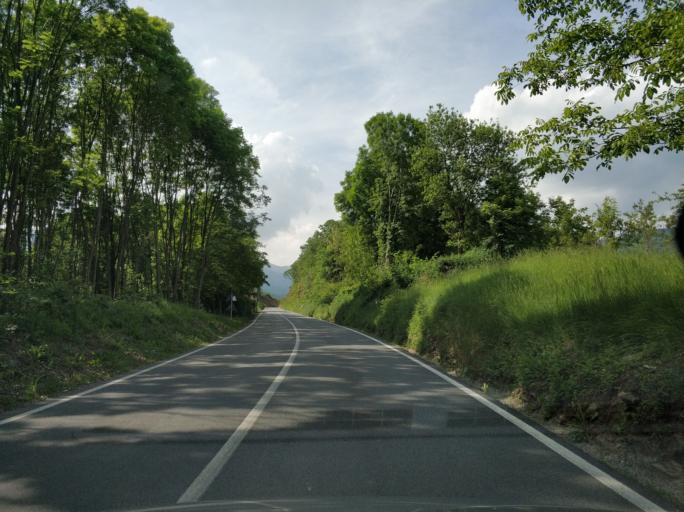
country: IT
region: Piedmont
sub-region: Provincia di Torino
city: Corio
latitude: 45.3014
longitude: 7.5420
